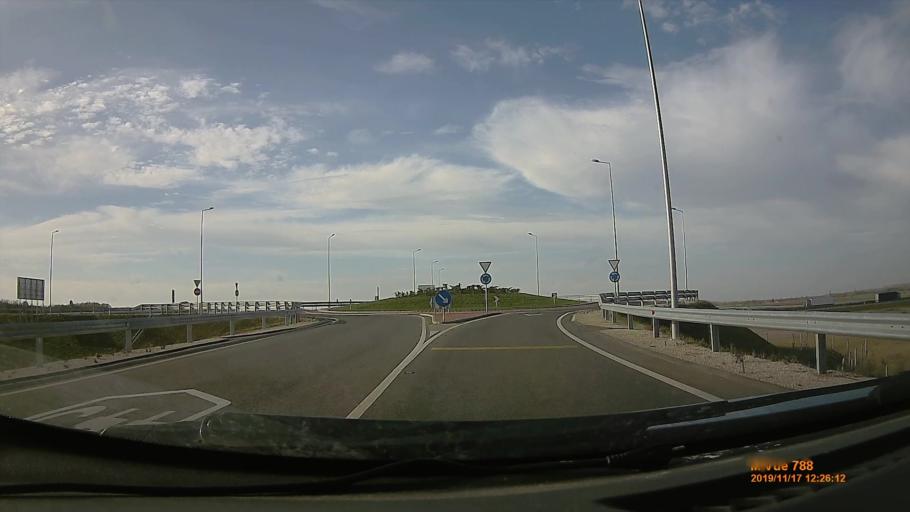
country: HU
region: Bacs-Kiskun
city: Kecskemet
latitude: 46.9325
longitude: 19.6203
